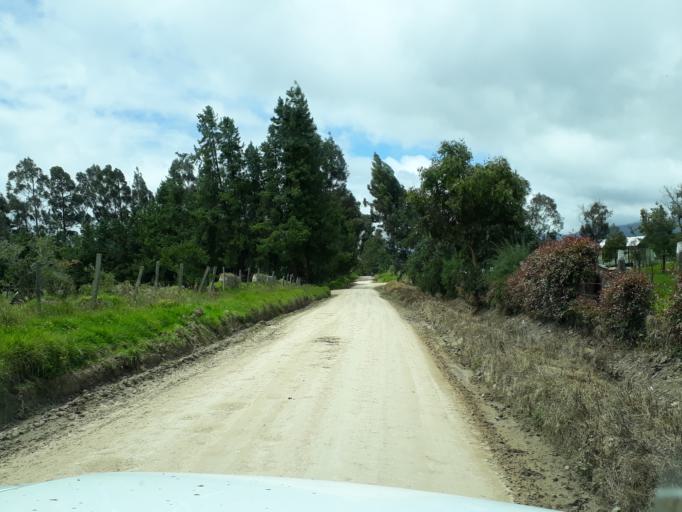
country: CO
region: Cundinamarca
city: Guasca
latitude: 4.8550
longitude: -73.8971
